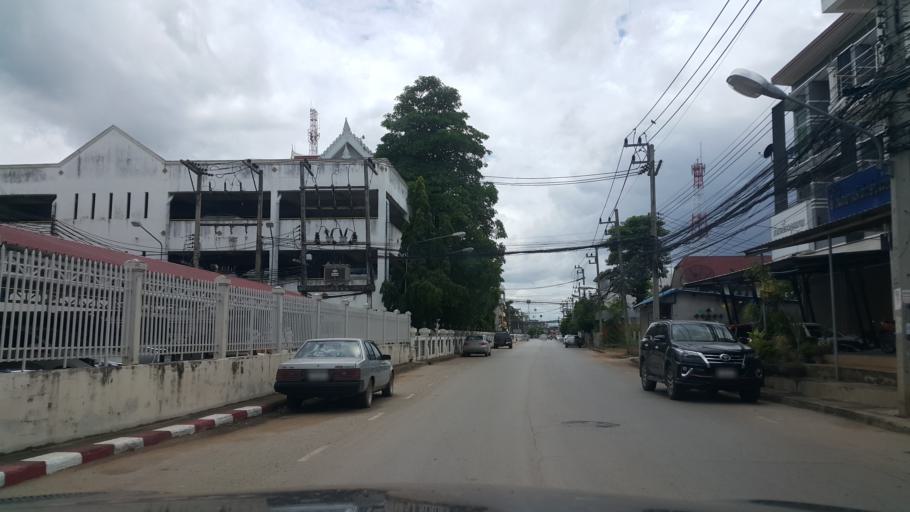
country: TH
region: Sukhothai
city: Sukhothai
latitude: 17.0056
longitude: 99.8280
